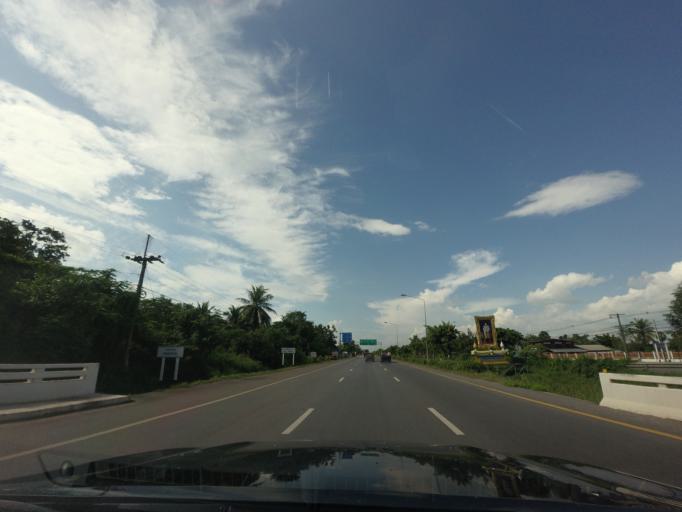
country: TH
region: Nong Khai
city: Sa Khrai
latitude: 17.6829
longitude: 102.7843
